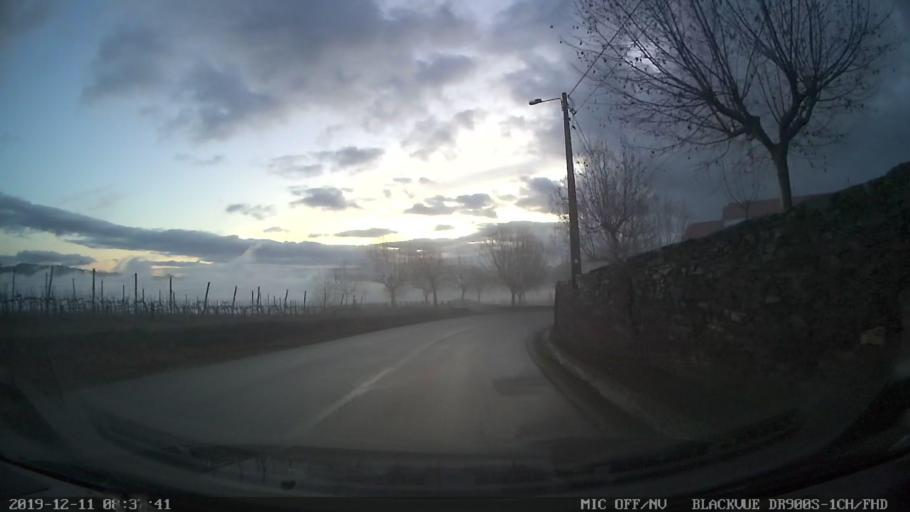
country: PT
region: Vila Real
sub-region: Sabrosa
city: Sabrosa
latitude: 41.2308
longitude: -7.5664
